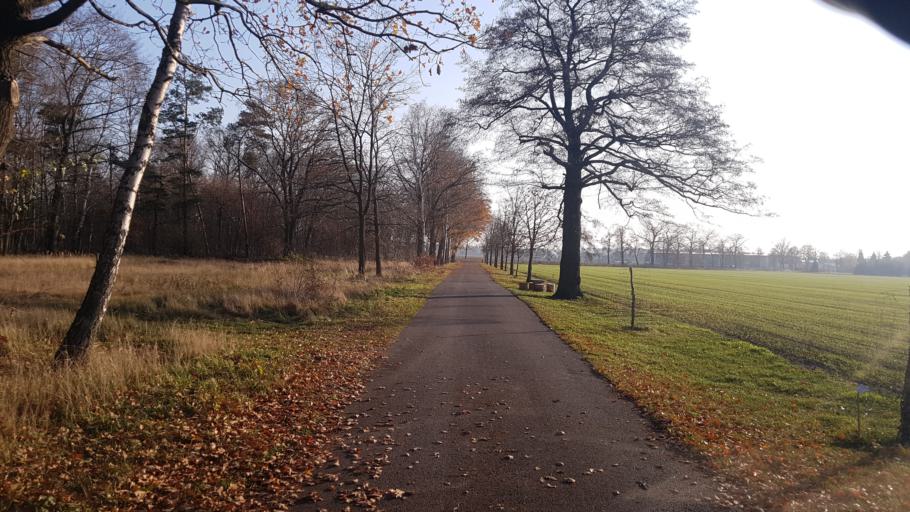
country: DE
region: Brandenburg
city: Tettau
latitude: 51.4387
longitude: 13.7303
